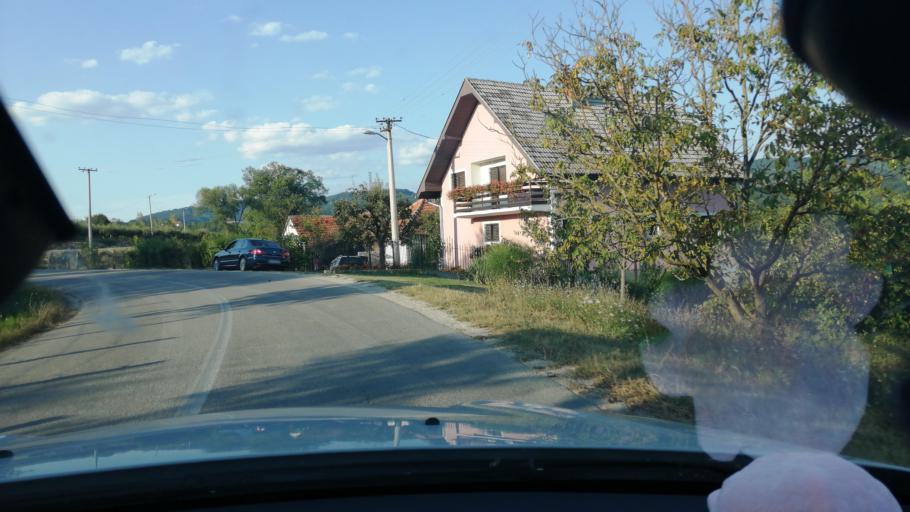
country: RS
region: Central Serbia
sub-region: Moravicki Okrug
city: Cacak
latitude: 43.8159
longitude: 20.2547
